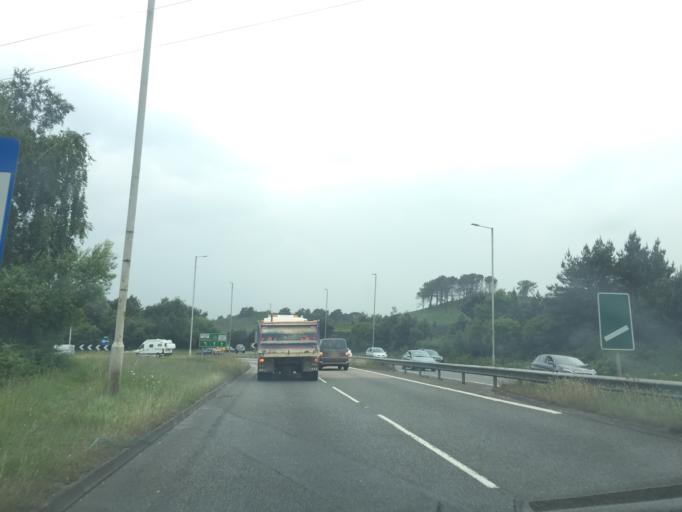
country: GB
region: England
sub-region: Poole
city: Canford Heath
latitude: 50.7539
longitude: -1.9469
